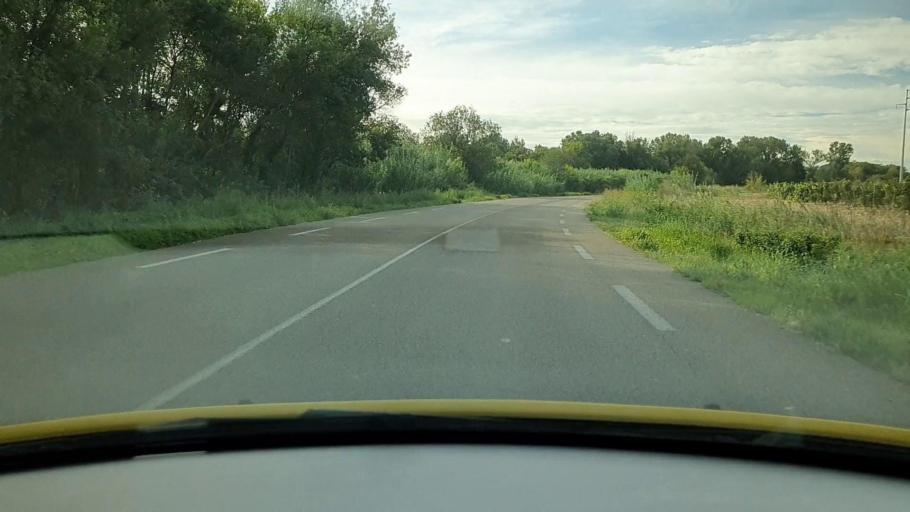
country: FR
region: Languedoc-Roussillon
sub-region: Departement du Gard
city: Bellegarde
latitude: 43.7517
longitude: 4.5297
